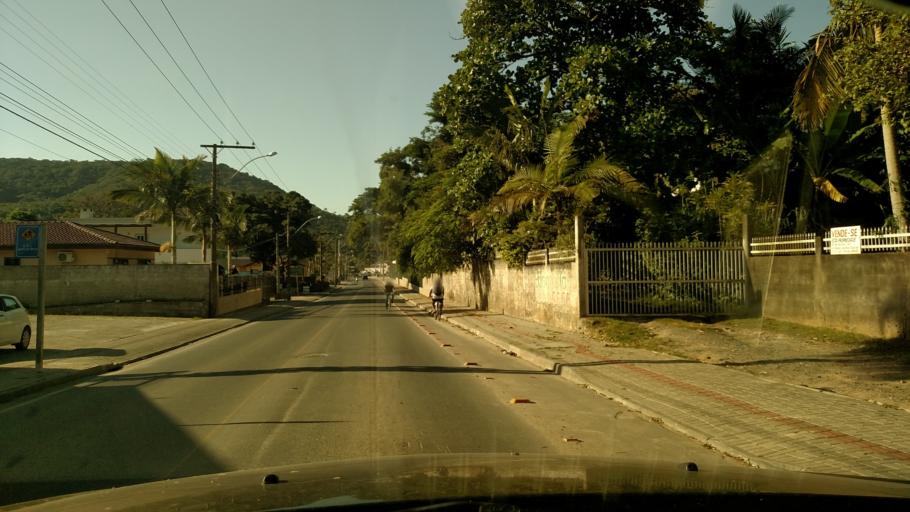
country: BR
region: Santa Catarina
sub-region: Porto Belo
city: Porto Belo
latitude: -27.1669
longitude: -48.5187
